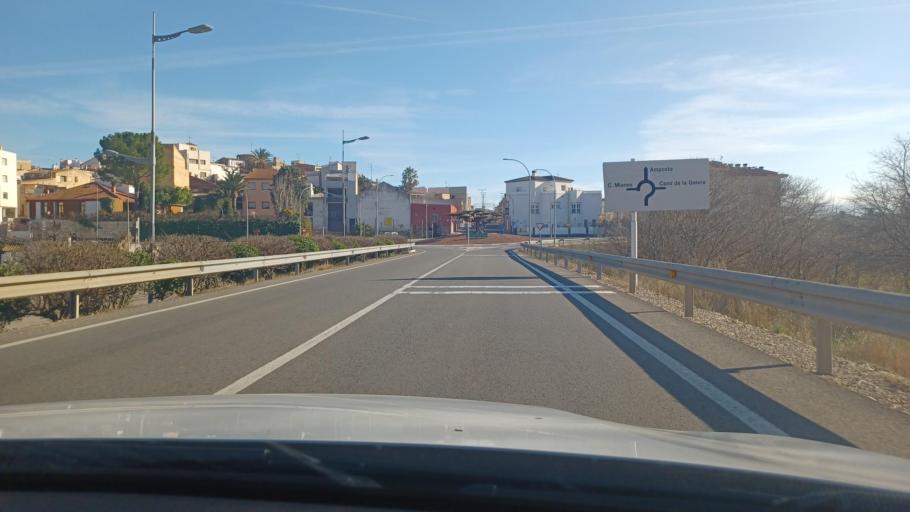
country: ES
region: Catalonia
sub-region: Provincia de Tarragona
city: Masdenverge
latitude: 40.7159
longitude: 0.5280
